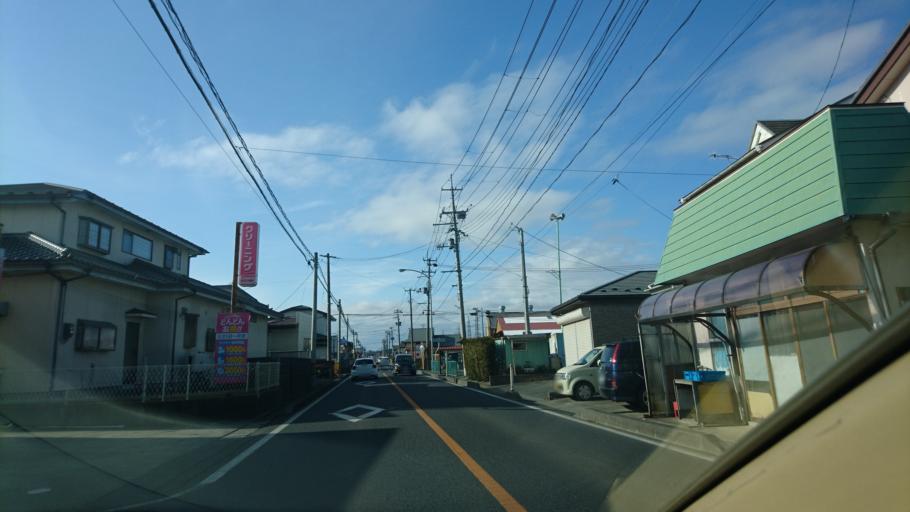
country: JP
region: Miyagi
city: Yamoto
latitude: 38.4725
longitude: 141.2247
